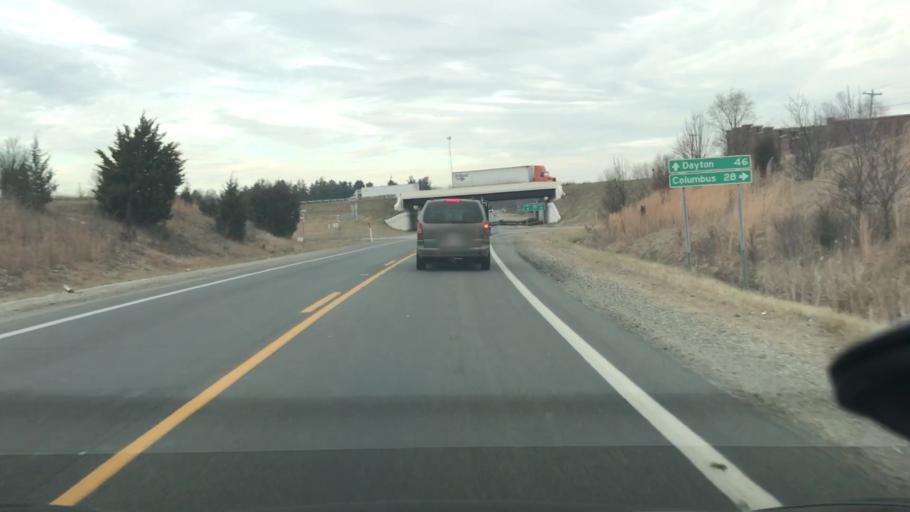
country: US
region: Ohio
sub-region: Madison County
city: Choctaw Lake
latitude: 39.9410
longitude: -83.4987
